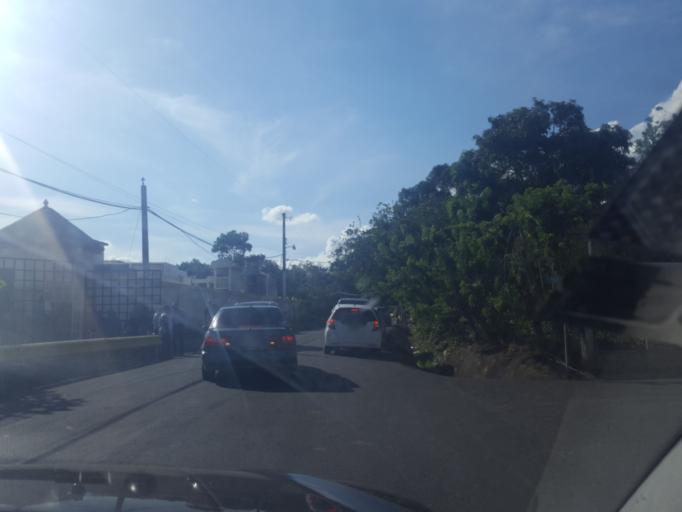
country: DO
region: La Vega
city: Rio Verde Arriba
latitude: 19.3456
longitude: -70.6219
